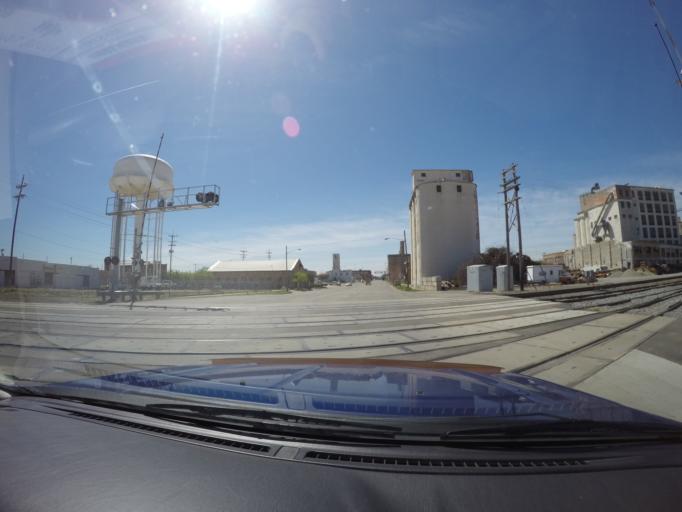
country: US
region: Kansas
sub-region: Saline County
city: Salina
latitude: 38.8503
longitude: -97.6091
